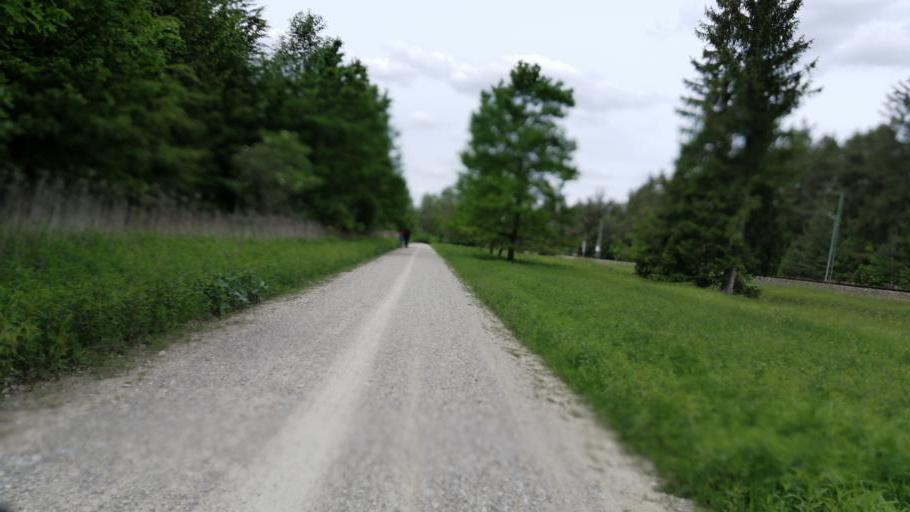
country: DE
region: Bavaria
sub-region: Upper Bavaria
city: Pullach im Isartal
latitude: 48.0617
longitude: 11.5632
